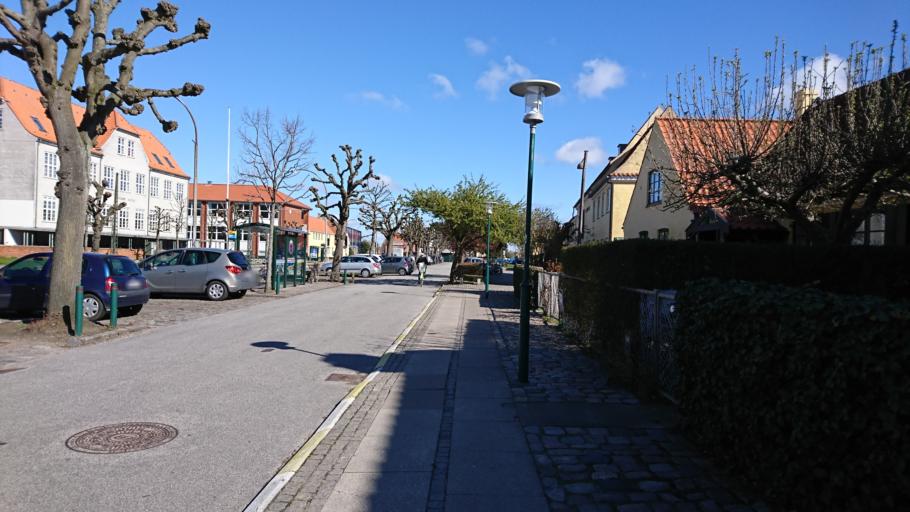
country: DK
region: Capital Region
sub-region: Dragor Kommune
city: Dragor
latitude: 55.5928
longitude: 12.6706
